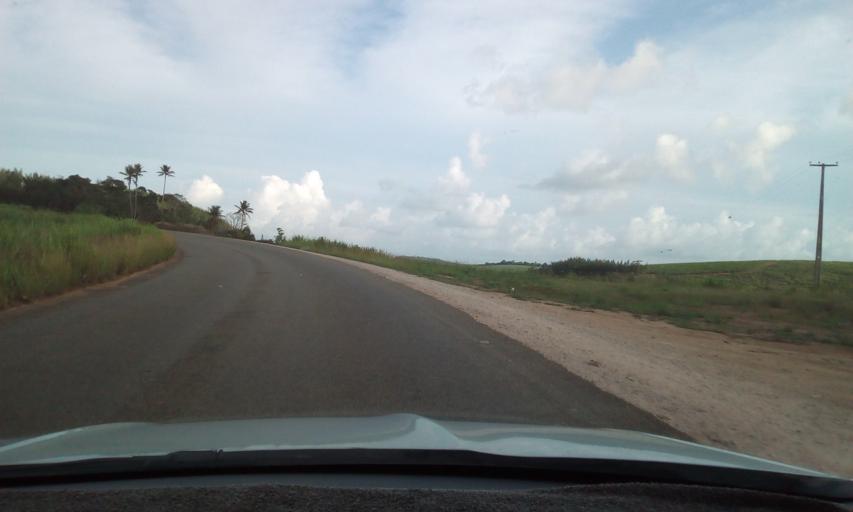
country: BR
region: Pernambuco
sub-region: Gloria Do Goita
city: Gloria do Goita
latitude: -7.9944
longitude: -35.2286
